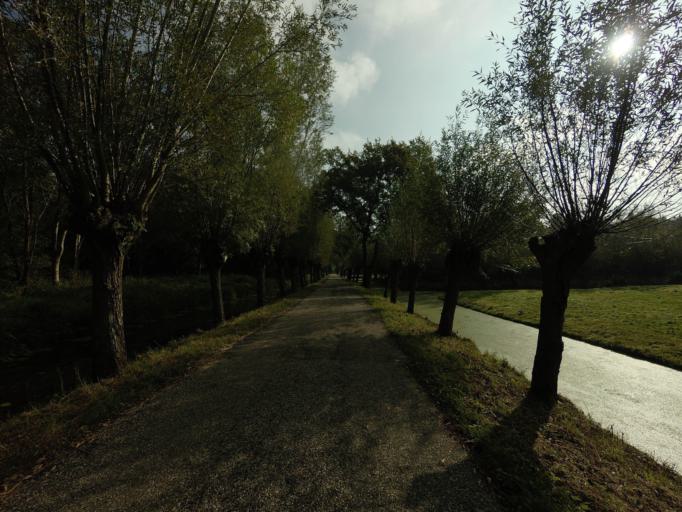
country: NL
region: Utrecht
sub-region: Gemeente Vianen
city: Vianen
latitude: 51.9619
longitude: 5.1051
